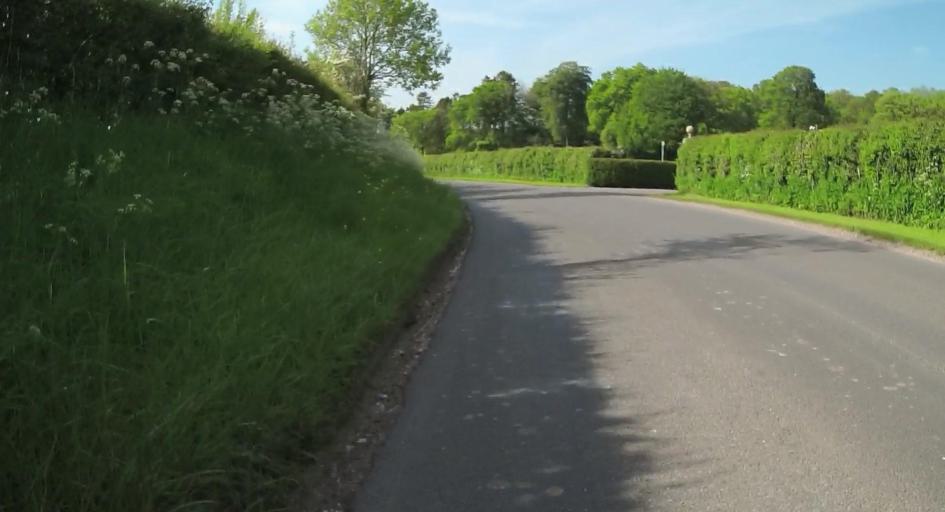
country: GB
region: England
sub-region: Hampshire
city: Four Marks
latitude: 51.1355
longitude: -1.0663
